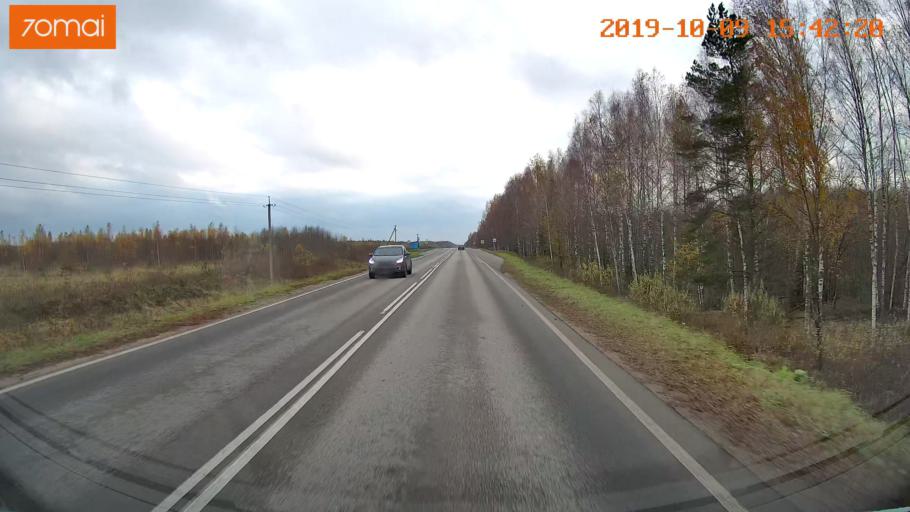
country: RU
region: Kostroma
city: Oktyabr'skiy
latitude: 57.8695
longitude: 41.1088
